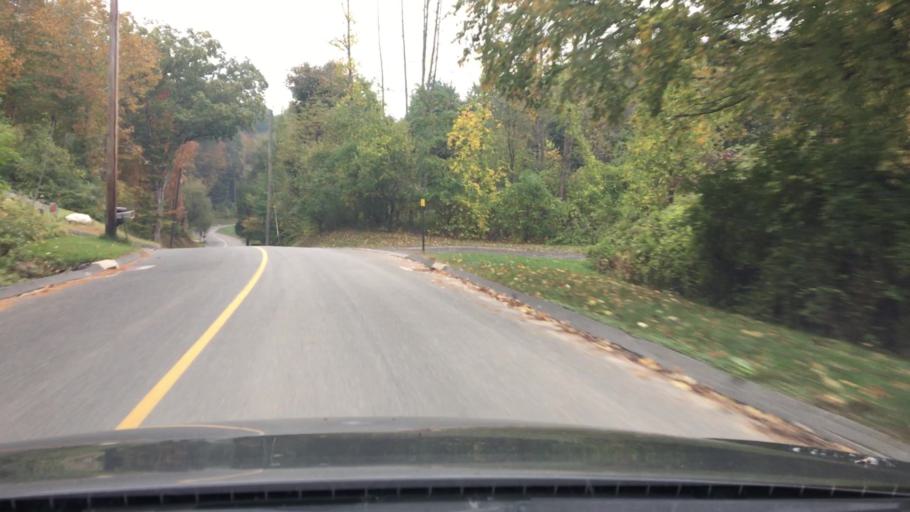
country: US
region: Connecticut
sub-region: New Haven County
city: Heritage Village
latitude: 41.5096
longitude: -73.2720
